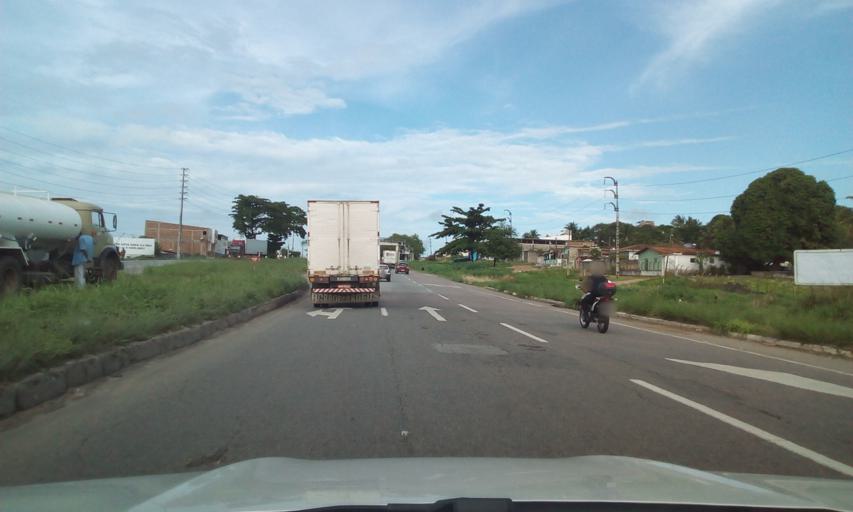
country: BR
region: Paraiba
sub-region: Bayeux
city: Bayeux
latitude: -7.1265
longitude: -34.9424
